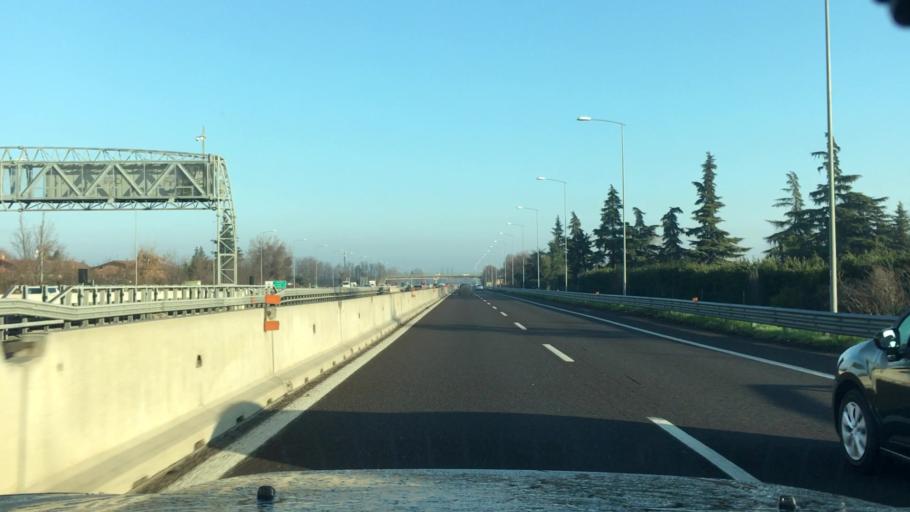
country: IT
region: Emilia-Romagna
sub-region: Provincia di Bologna
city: Casalecchio di Reno
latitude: 44.4977
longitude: 11.2717
